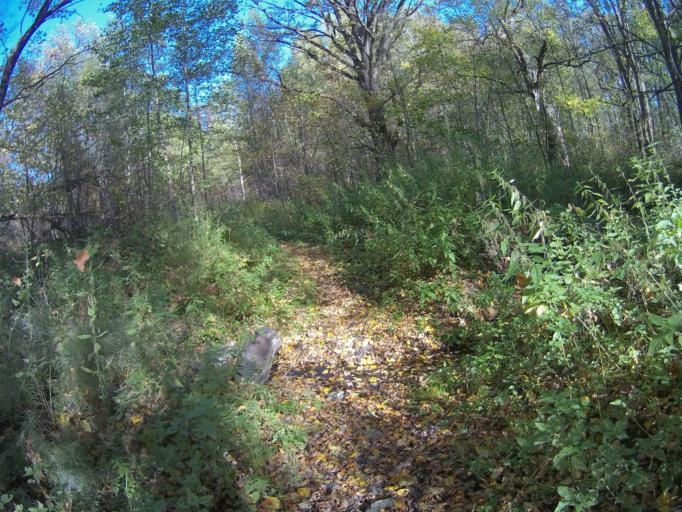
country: RU
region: Vladimir
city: Raduzhnyy
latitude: 56.0445
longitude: 40.3742
